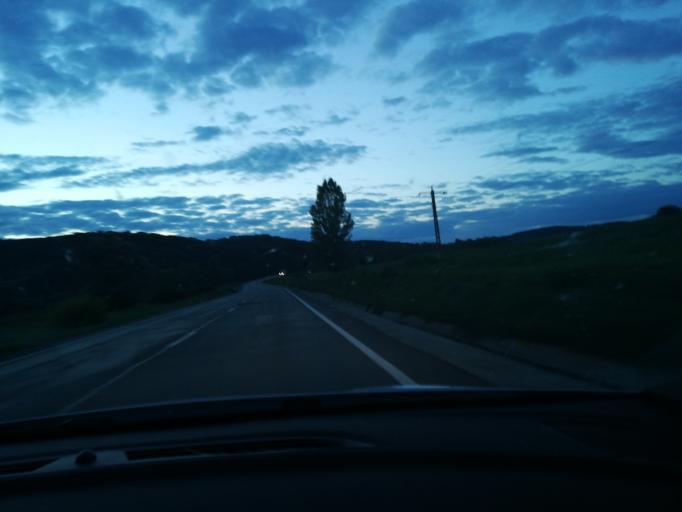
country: RO
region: Brasov
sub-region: Comuna Bunesti
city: Bunesti
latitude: 46.1304
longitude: 25.0180
